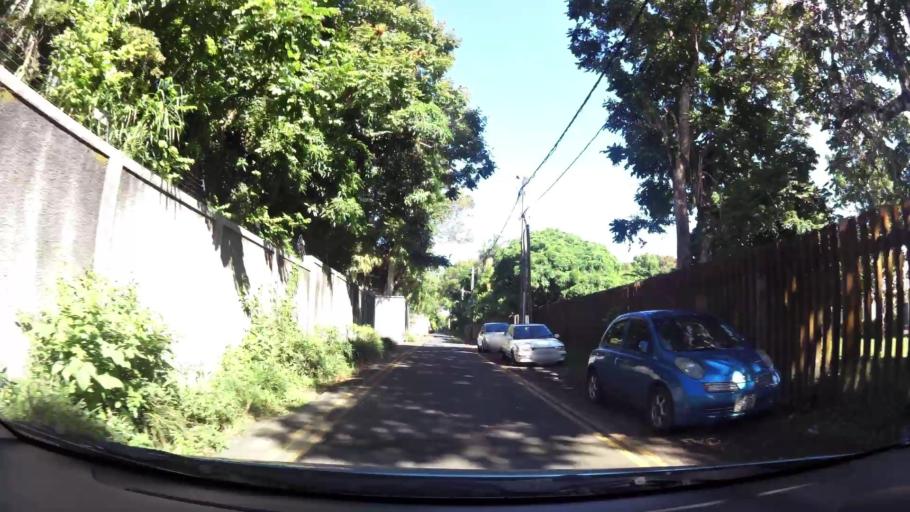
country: MU
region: Plaines Wilhems
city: Vacoas
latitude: -20.2979
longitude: 57.4973
